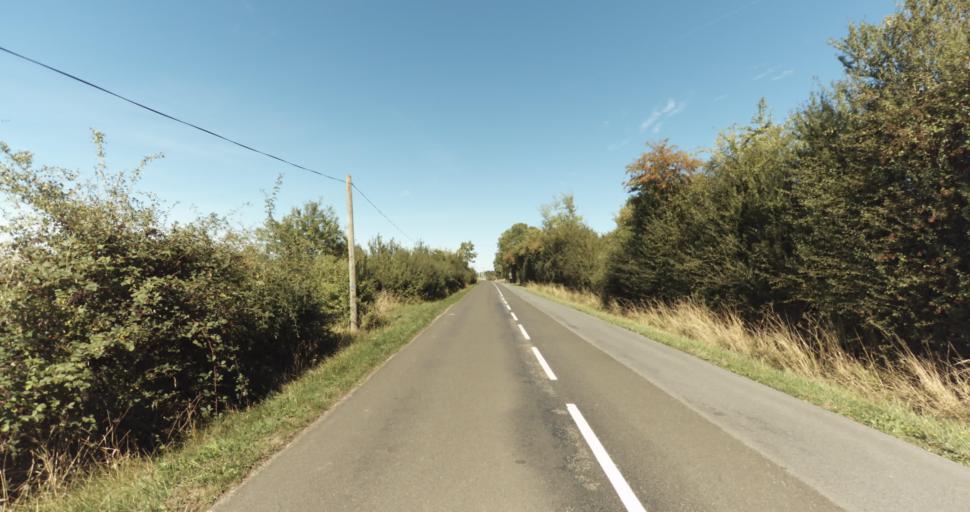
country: FR
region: Lower Normandy
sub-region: Departement de l'Orne
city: Gace
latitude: 48.7947
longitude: 0.2163
